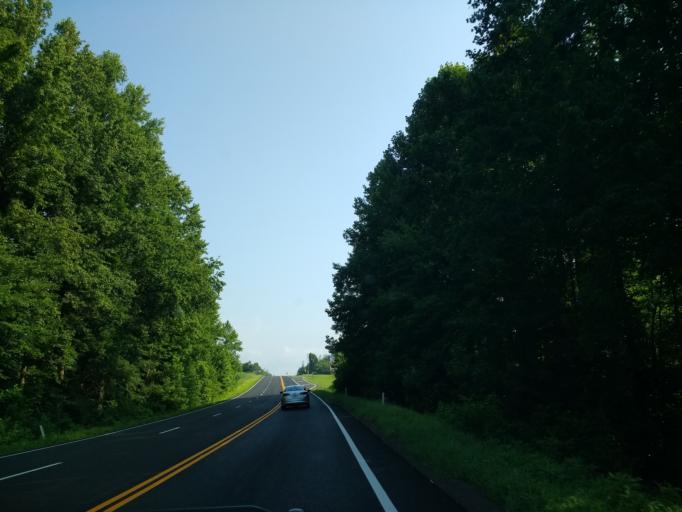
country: US
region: Georgia
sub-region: White County
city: Cleveland
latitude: 34.4963
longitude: -83.7559
